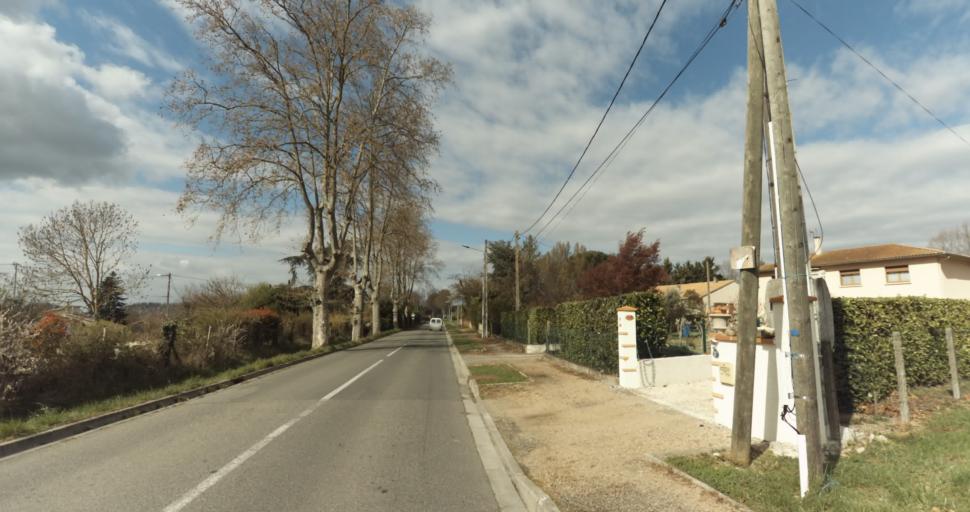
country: FR
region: Midi-Pyrenees
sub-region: Departement de la Haute-Garonne
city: Auterive
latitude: 43.3580
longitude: 1.4767
